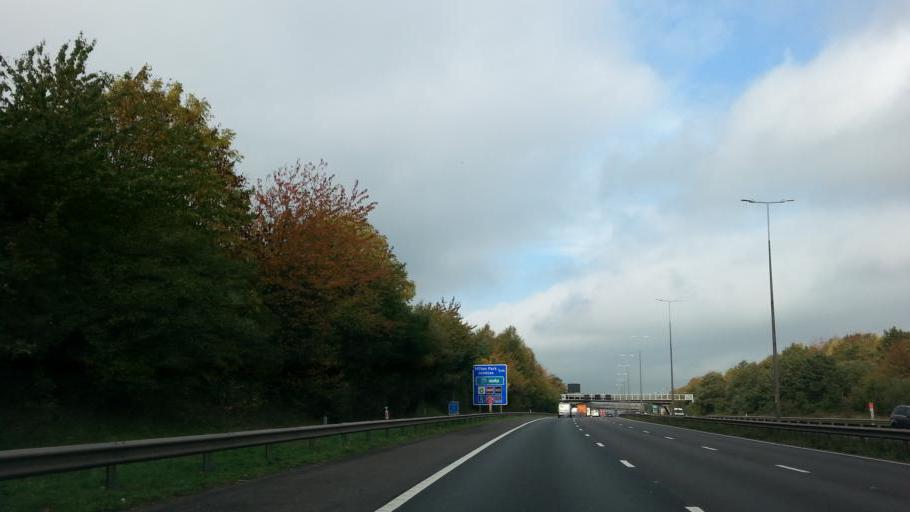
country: GB
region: England
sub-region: Staffordshire
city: Essington
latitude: 52.6318
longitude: -2.0504
